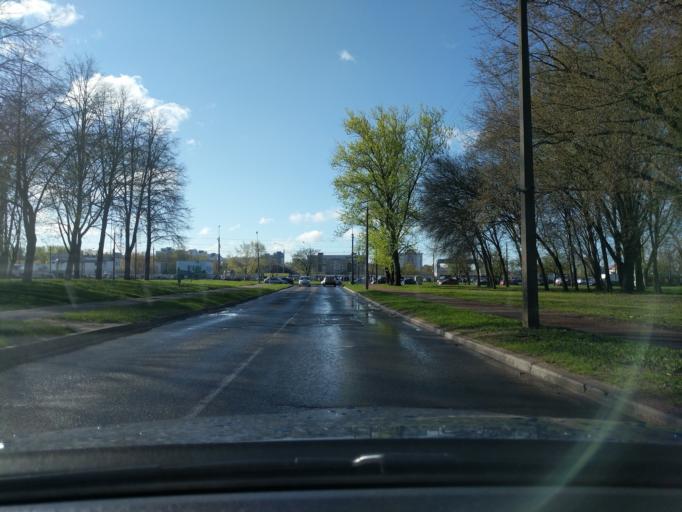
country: BY
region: Minsk
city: Novoye Medvezhino
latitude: 53.8991
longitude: 27.5069
